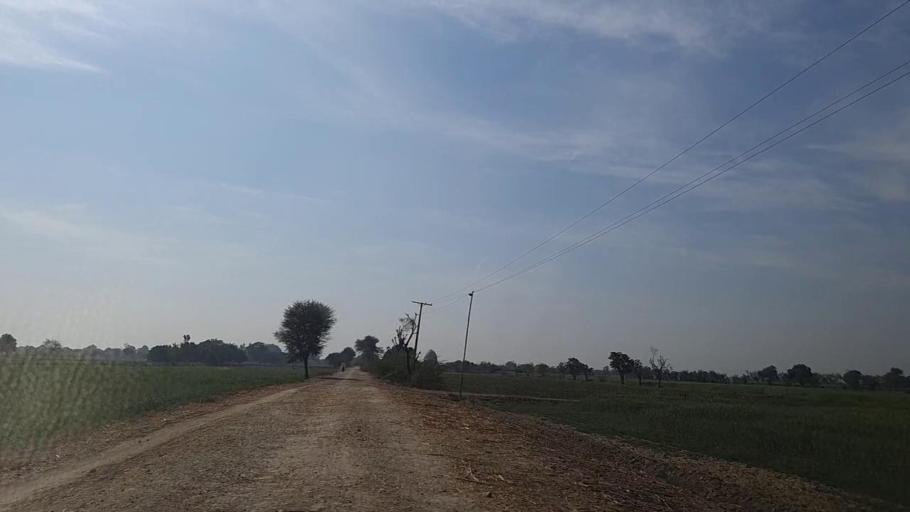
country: PK
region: Sindh
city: Mirpur Khas
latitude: 25.4765
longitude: 68.9745
